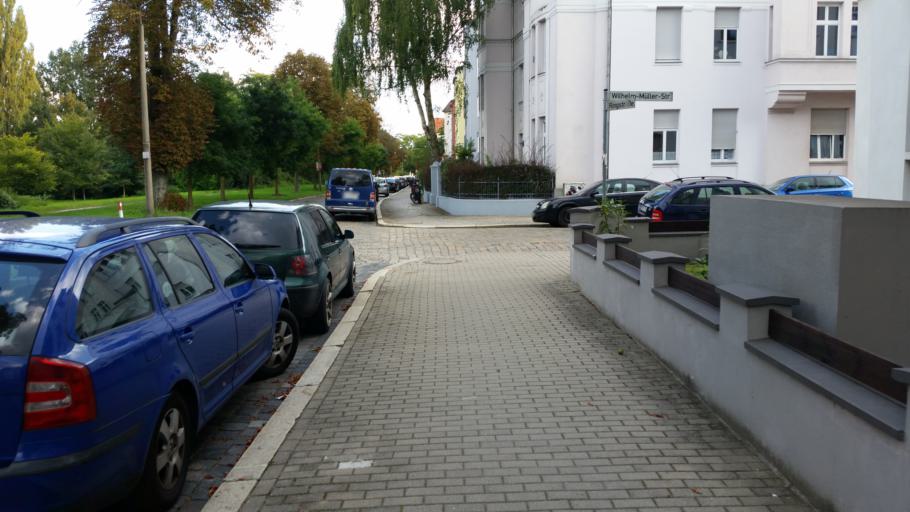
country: DE
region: Saxony-Anhalt
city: Dessau
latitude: 51.8454
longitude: 12.2468
